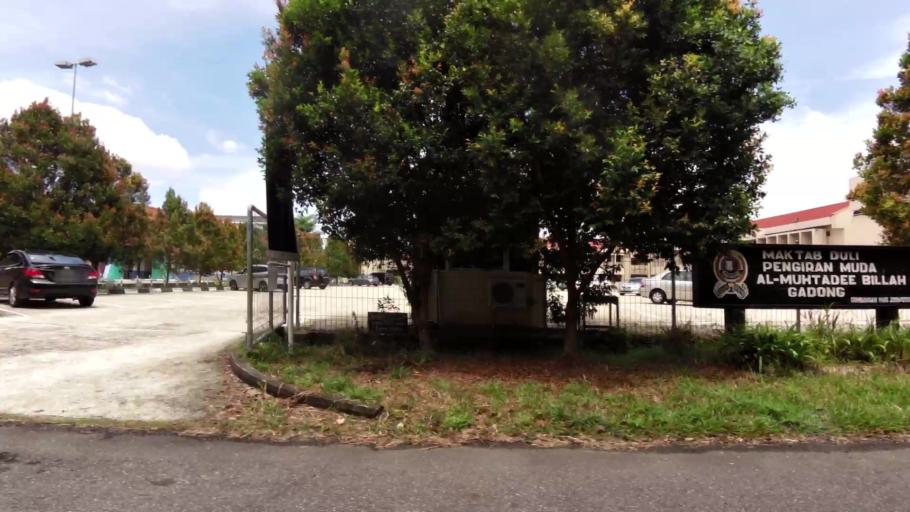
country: BN
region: Brunei and Muara
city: Bandar Seri Begawan
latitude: 4.9029
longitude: 114.9116
